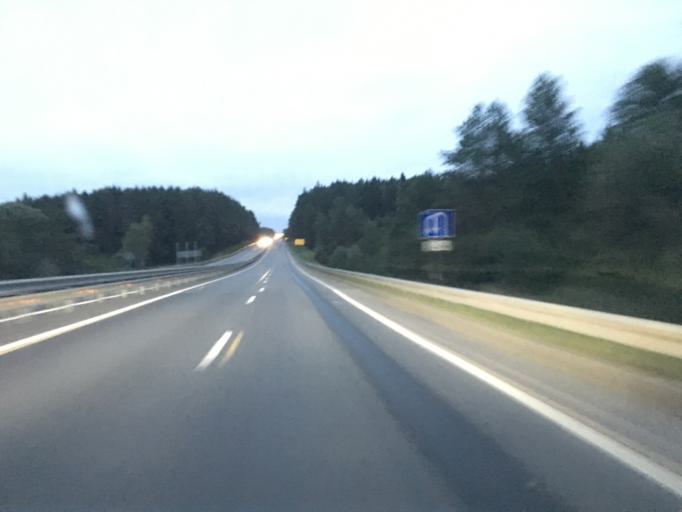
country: RU
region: Kaluga
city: Maloyaroslavets
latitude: 54.9597
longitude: 36.4615
